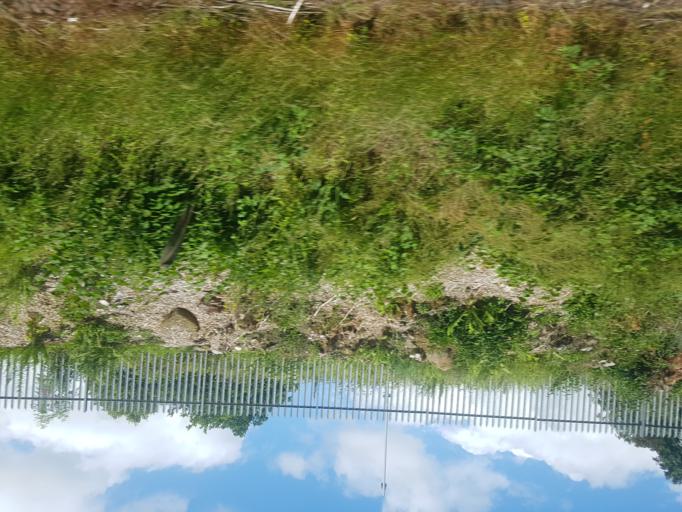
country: GB
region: Scotland
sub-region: Falkirk
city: Falkirk
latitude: 55.9847
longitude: -3.7754
